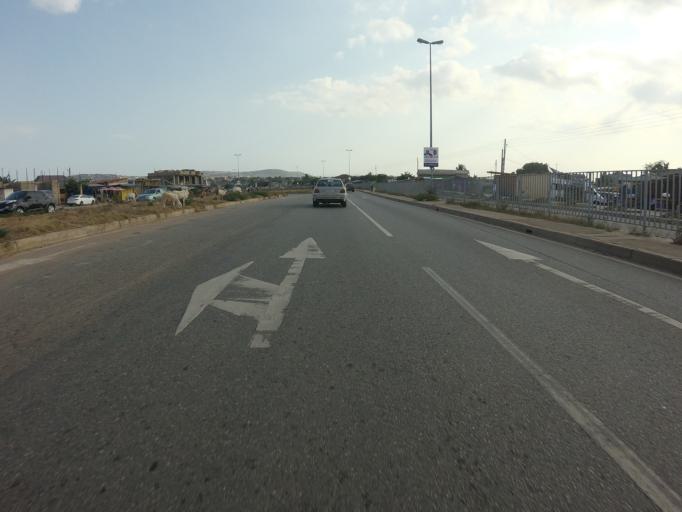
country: GH
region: Greater Accra
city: Achiaman
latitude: 5.6445
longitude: -0.3107
